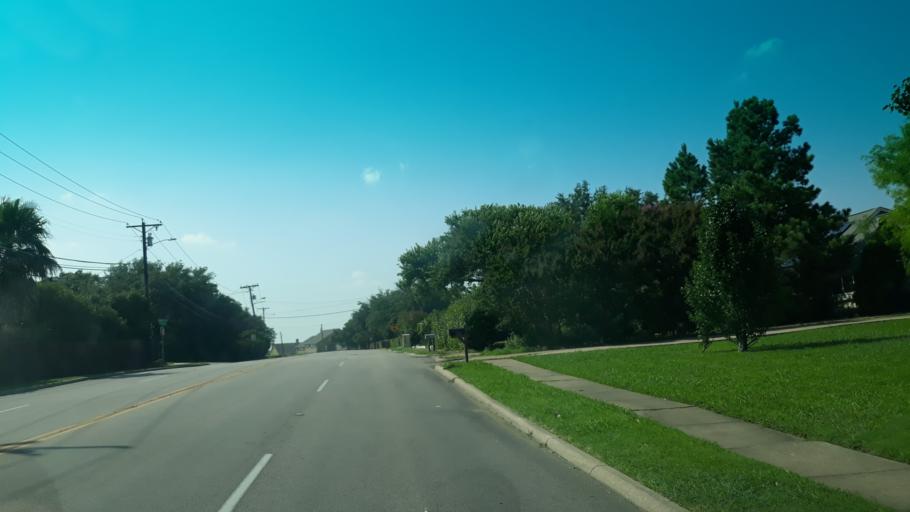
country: US
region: Texas
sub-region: Dallas County
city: Irving
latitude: 32.8573
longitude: -96.9801
